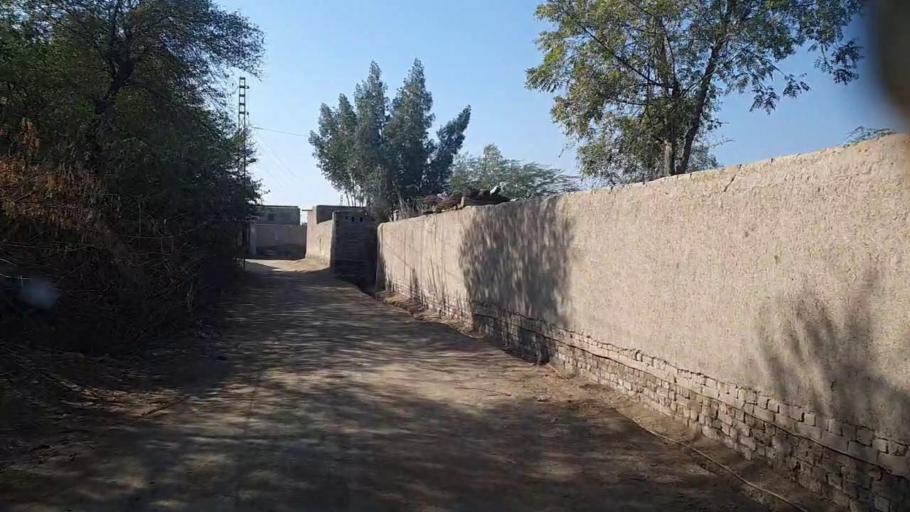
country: PK
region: Sindh
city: Khairpur
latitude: 27.9558
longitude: 69.6856
